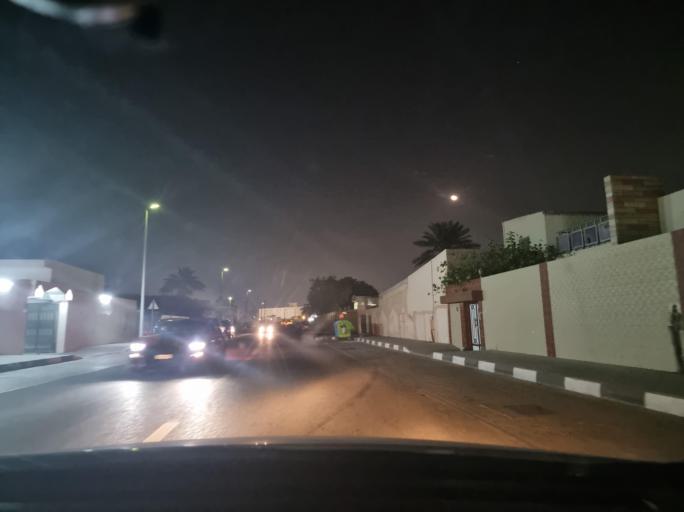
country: AE
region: Ash Shariqah
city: Sharjah
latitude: 25.3699
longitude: 55.4232
